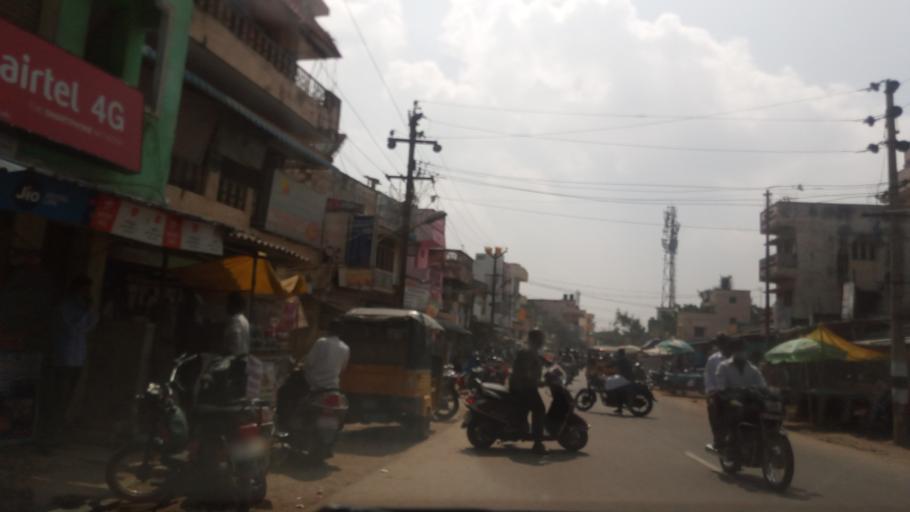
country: IN
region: Tamil Nadu
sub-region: Vellore
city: Arakkonam
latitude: 13.0799
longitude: 79.6714
